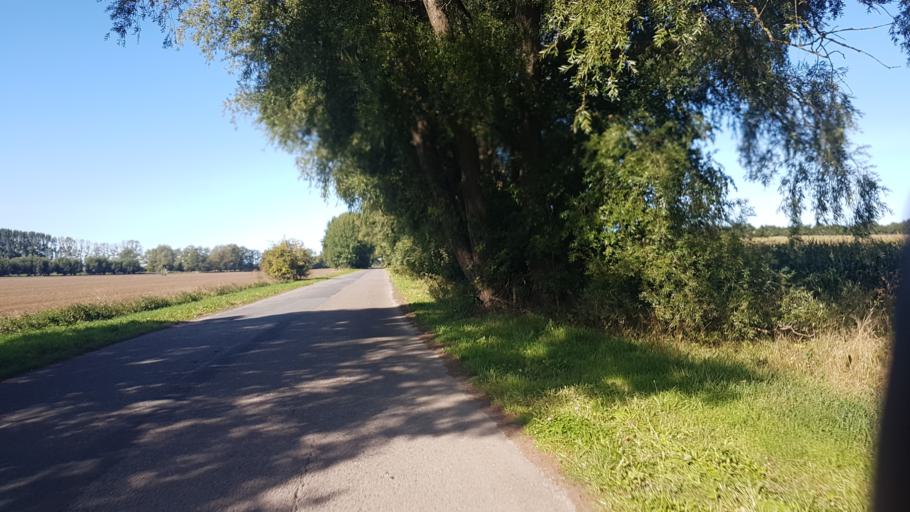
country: DE
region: Mecklenburg-Vorpommern
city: Sagard
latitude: 54.5200
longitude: 13.5276
